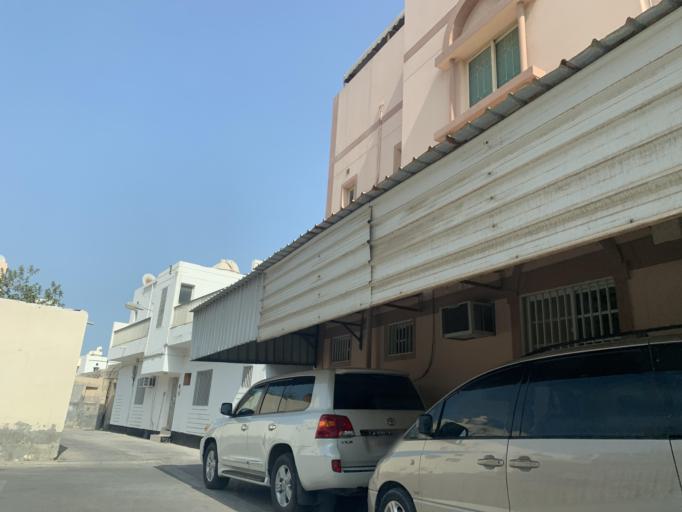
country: BH
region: Muharraq
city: Al Hadd
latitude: 26.2715
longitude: 50.6538
